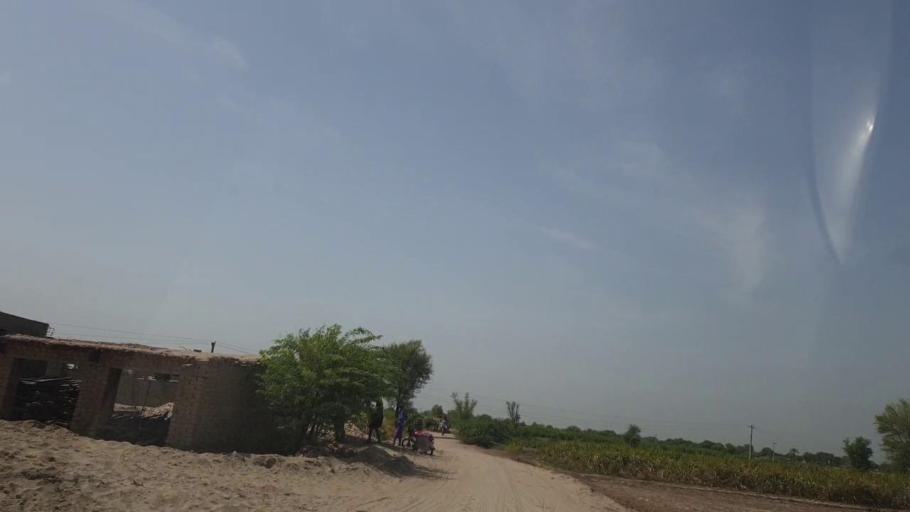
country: PK
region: Sindh
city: Gambat
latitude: 27.3789
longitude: 68.5834
